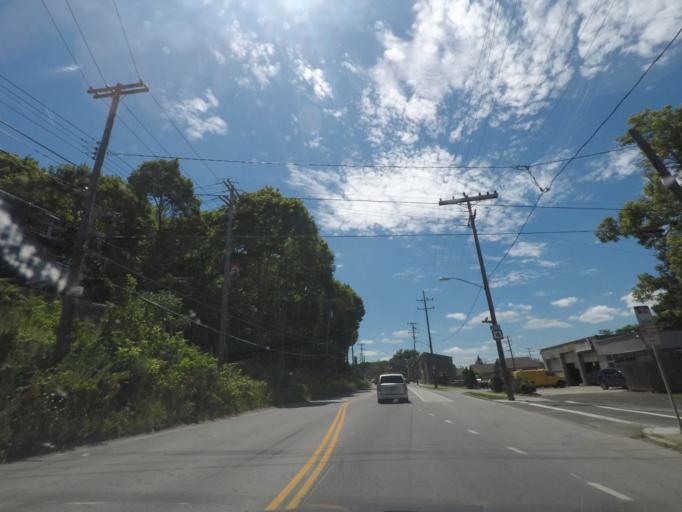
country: US
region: New York
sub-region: Rensselaer County
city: Troy
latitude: 42.7077
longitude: -73.6976
